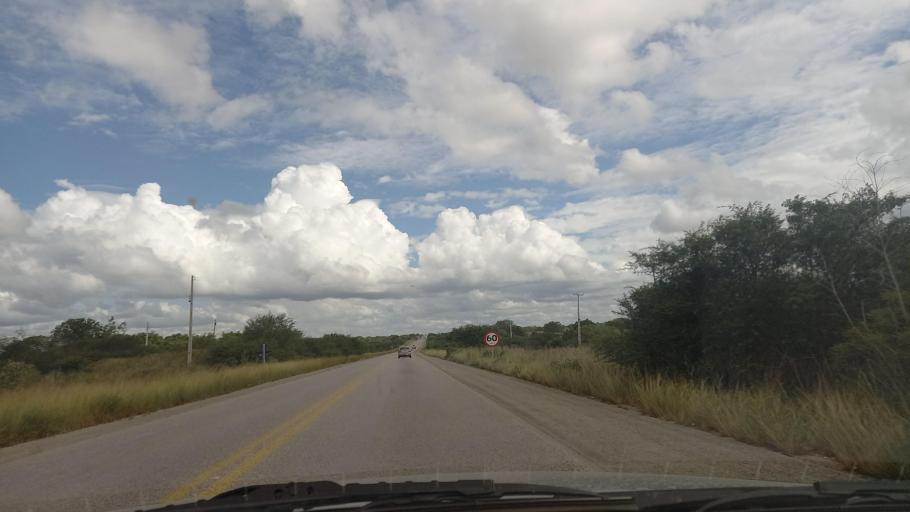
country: BR
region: Pernambuco
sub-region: Cachoeirinha
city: Cachoeirinha
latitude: -8.4302
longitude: -36.1996
